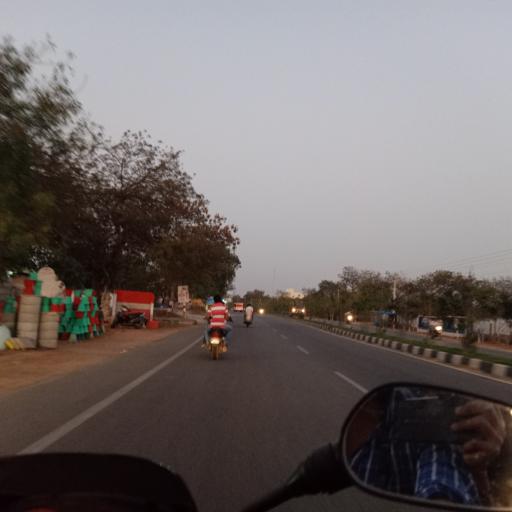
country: IN
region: Telangana
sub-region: Rangareddi
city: Secunderabad
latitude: 17.5618
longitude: 78.5478
